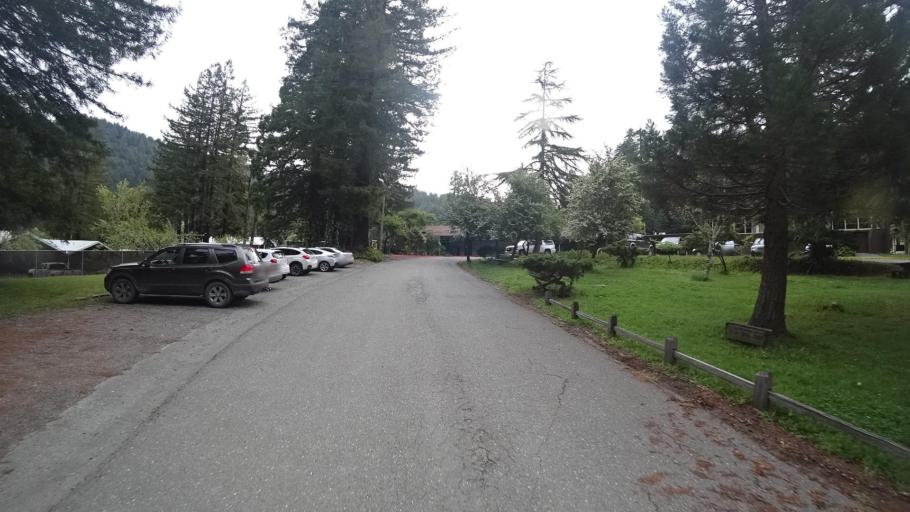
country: US
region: California
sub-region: Humboldt County
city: Redway
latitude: 40.3205
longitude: -123.9246
